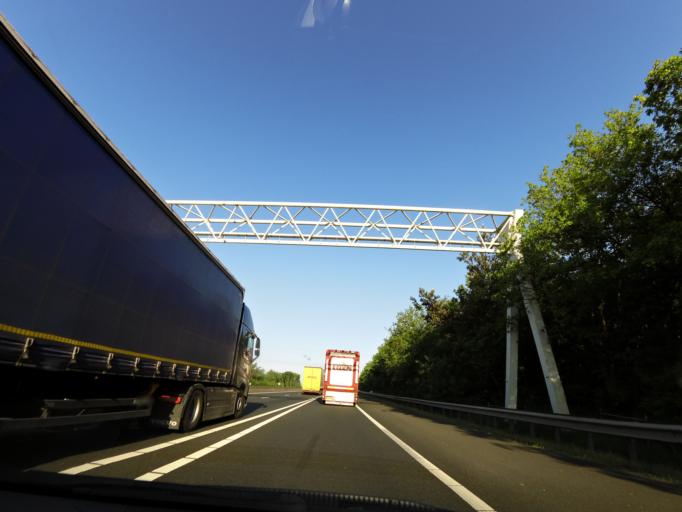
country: NL
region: Limburg
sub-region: Gemeente Venlo
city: Tegelen
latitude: 51.3935
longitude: 6.1151
